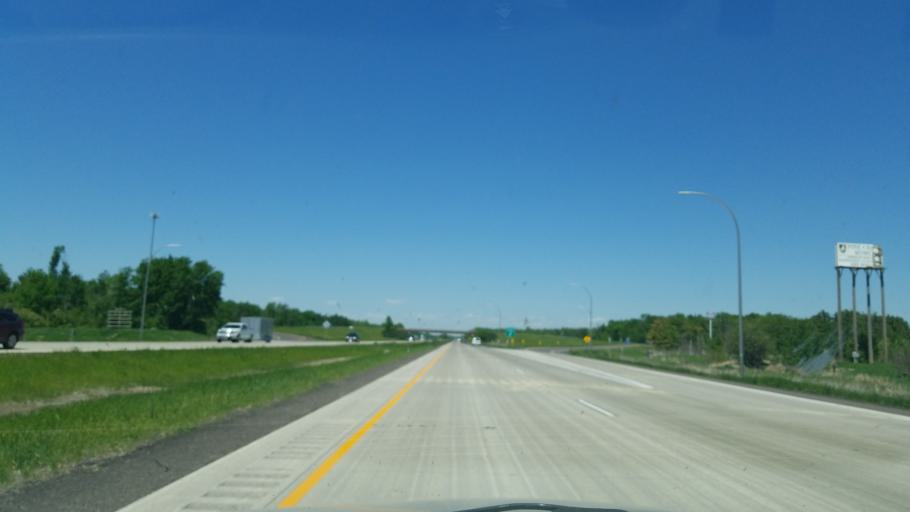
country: US
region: Minnesota
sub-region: Pine County
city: Pine City
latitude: 45.9002
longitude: -92.9667
